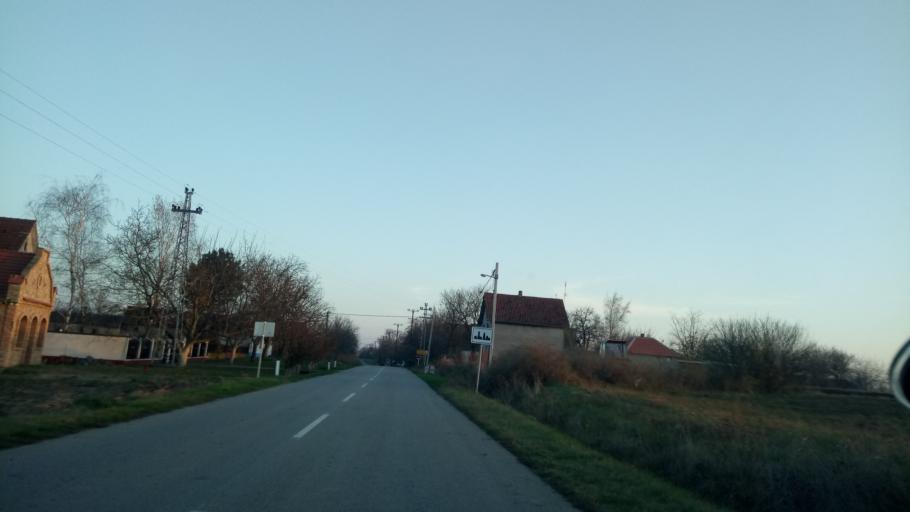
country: RS
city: Surduk
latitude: 45.0841
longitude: 20.3071
